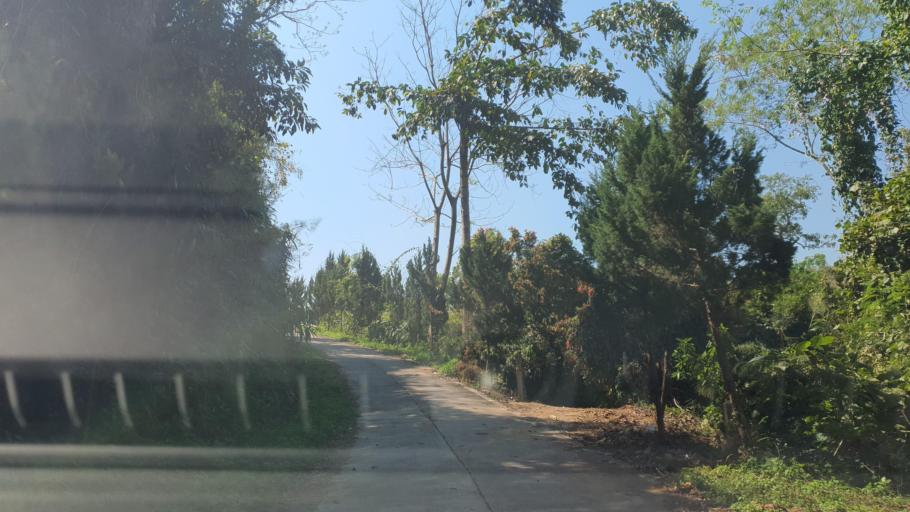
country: TH
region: Lampang
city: Wang Nuea
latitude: 19.1855
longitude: 99.4957
